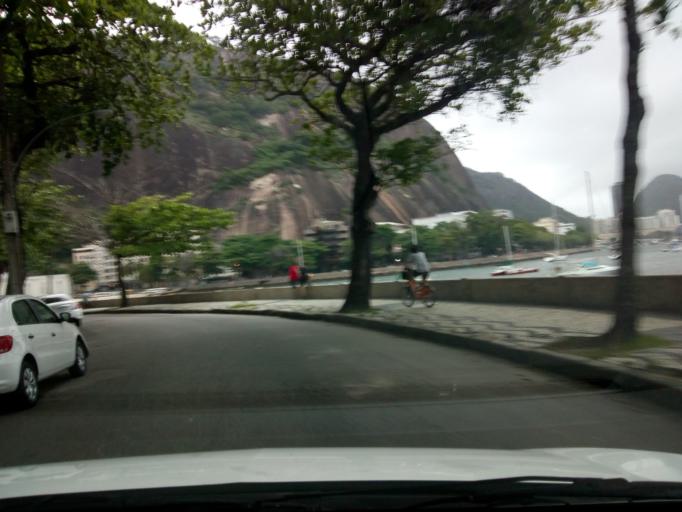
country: BR
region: Rio de Janeiro
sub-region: Rio De Janeiro
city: Rio de Janeiro
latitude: -22.9458
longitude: -43.1636
